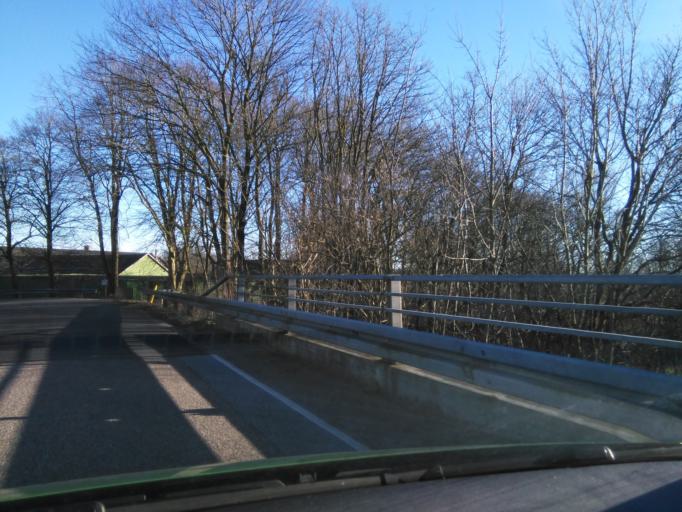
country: DK
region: North Denmark
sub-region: Mariagerfjord Kommune
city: Hobro
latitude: 56.6675
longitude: 9.8107
